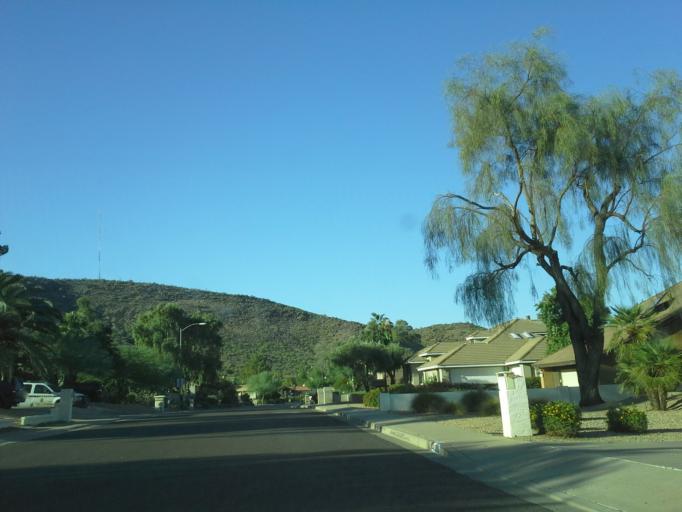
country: US
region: Arizona
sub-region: Maricopa County
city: Glendale
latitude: 33.6056
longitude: -112.0883
